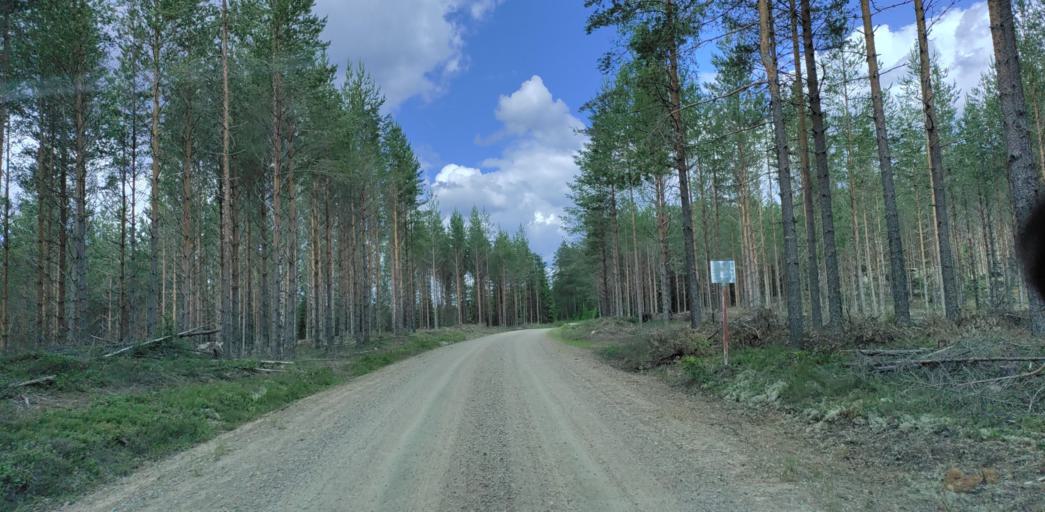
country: SE
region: Vaermland
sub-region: Hagfors Kommun
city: Ekshaerad
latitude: 60.0660
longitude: 13.2902
